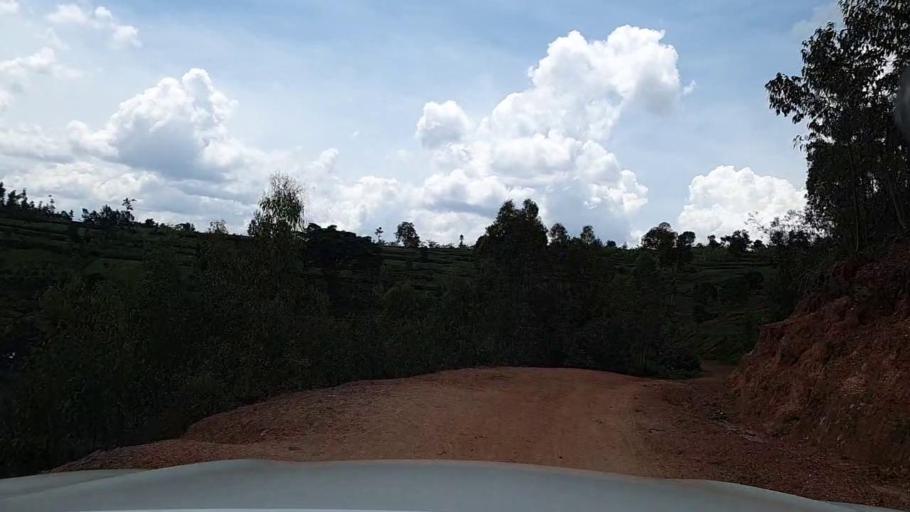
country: RW
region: Southern Province
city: Butare
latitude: -2.7558
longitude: 29.7483
